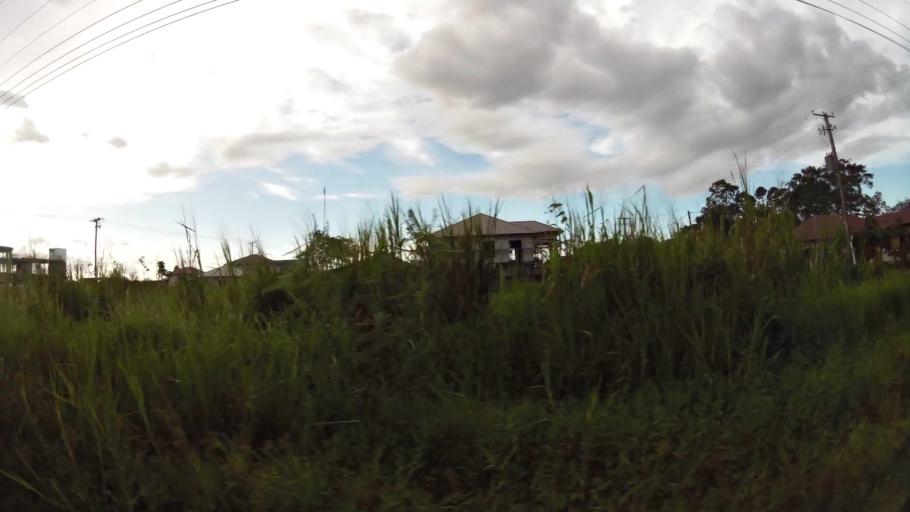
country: SR
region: Paramaribo
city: Paramaribo
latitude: 5.8582
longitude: -55.1795
